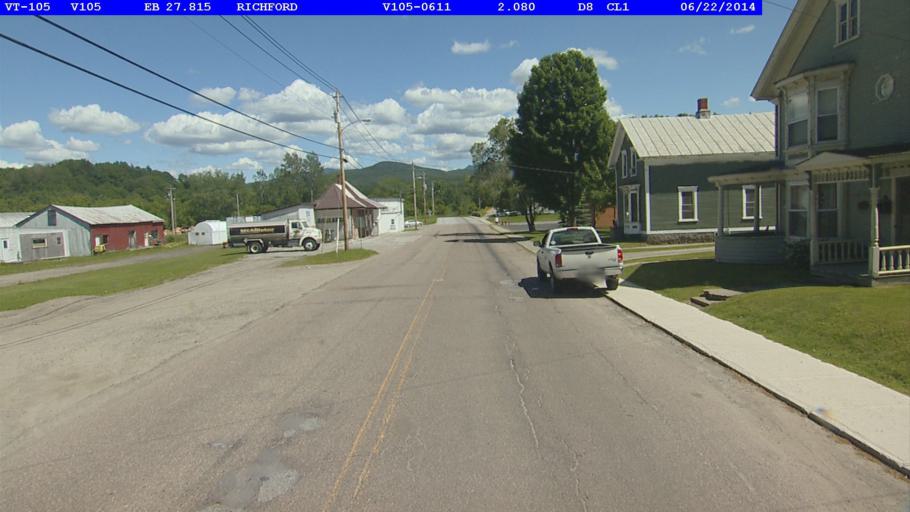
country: US
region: Vermont
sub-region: Franklin County
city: Richford
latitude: 44.9912
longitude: -72.6713
